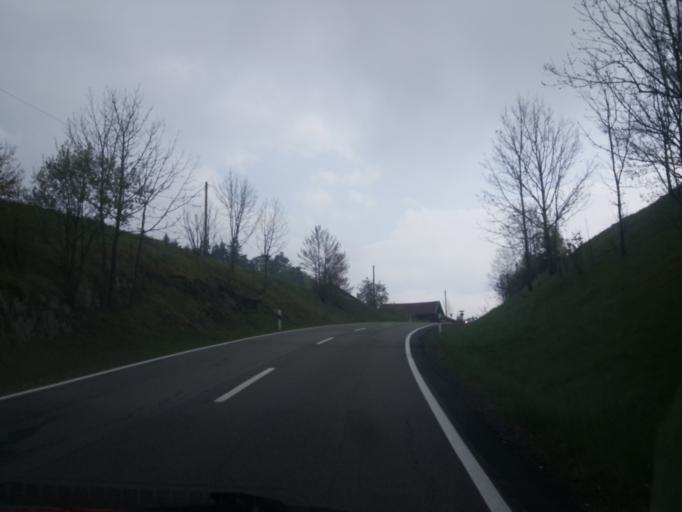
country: DE
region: Bavaria
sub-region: Lower Bavaria
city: Geiersthal
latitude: 49.0537
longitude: 12.9524
